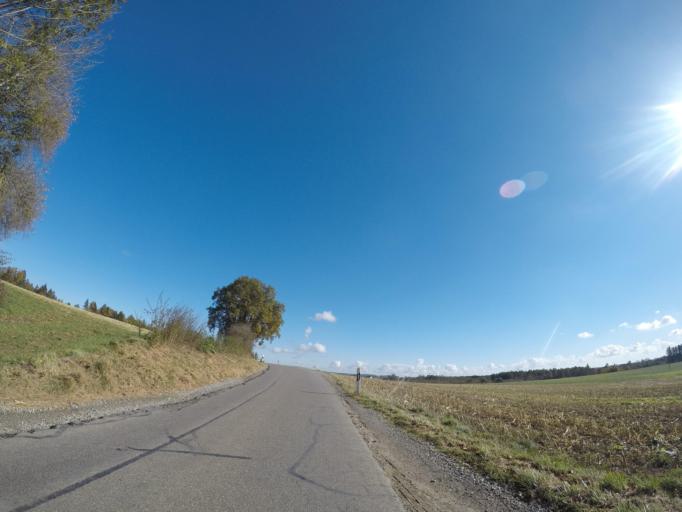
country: DE
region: Baden-Wuerttemberg
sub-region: Tuebingen Region
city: Durnau
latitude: 48.0807
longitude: 9.5765
